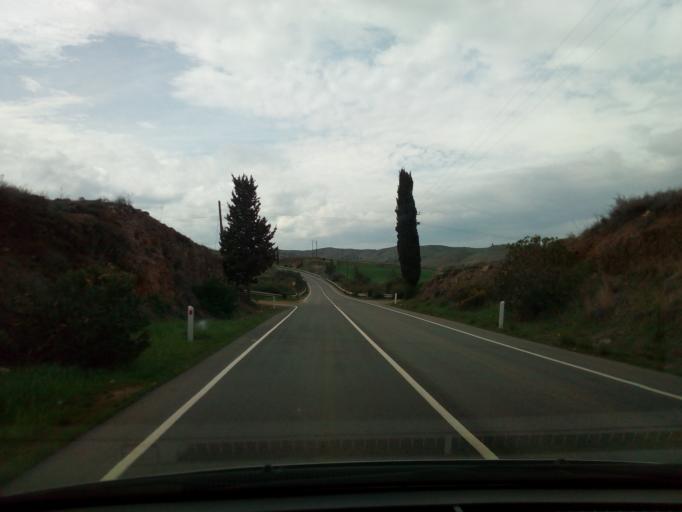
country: CY
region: Lefkosia
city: Astromeritis
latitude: 35.0847
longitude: 32.9544
